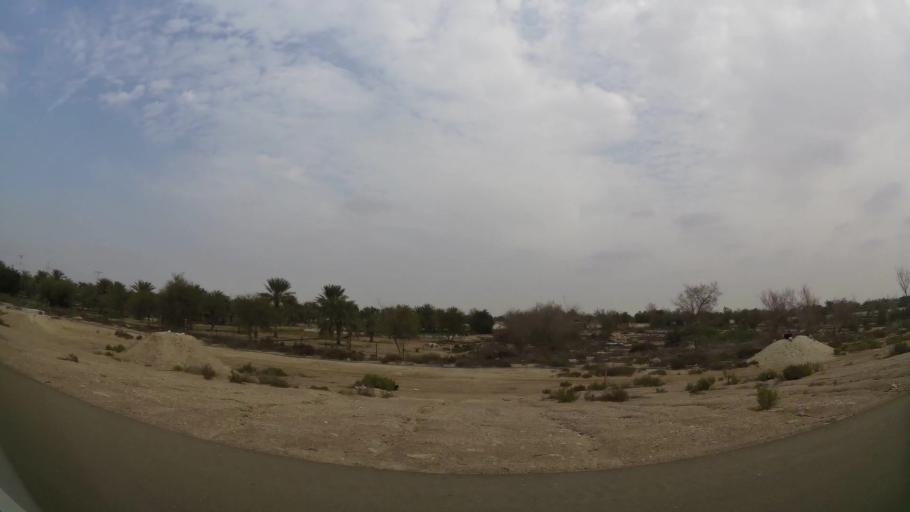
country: AE
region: Abu Dhabi
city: Abu Dhabi
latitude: 24.6318
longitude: 54.7027
